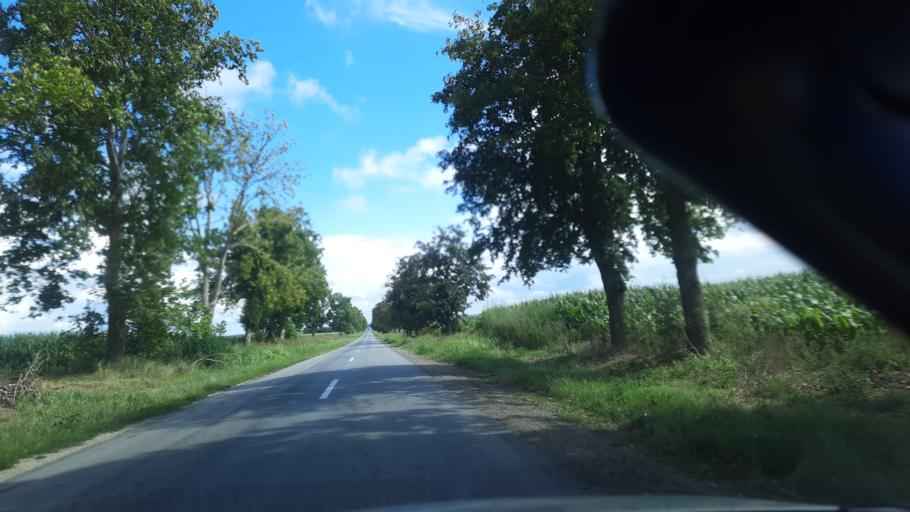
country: RS
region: Autonomna Pokrajina Vojvodina
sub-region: Sremski Okrug
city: Sremska Mitrovica
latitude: 45.0763
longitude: 19.5886
